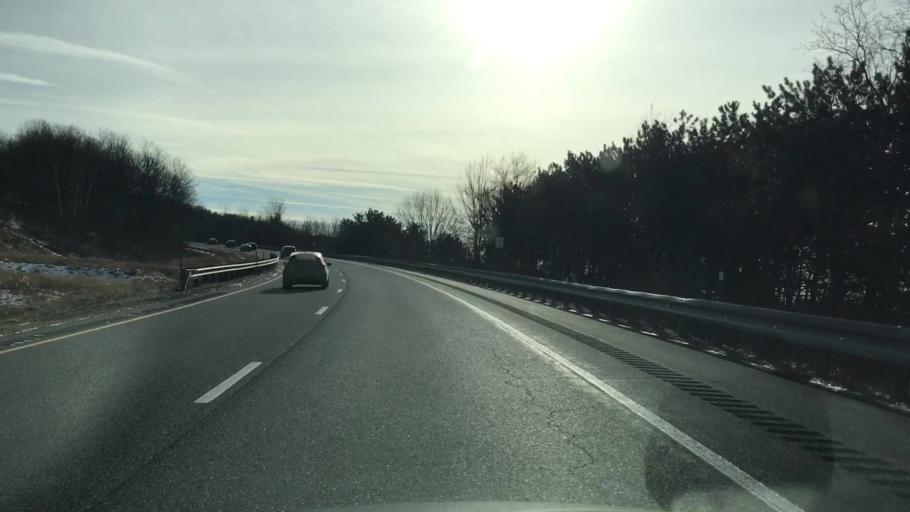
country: US
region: New Hampshire
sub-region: Sullivan County
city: Grantham
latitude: 43.4699
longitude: -72.1034
